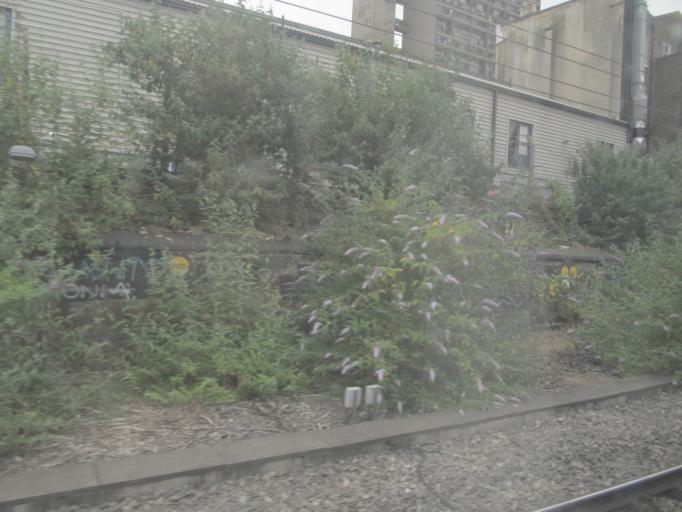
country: GB
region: England
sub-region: Greater London
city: Bayswater
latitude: 51.5232
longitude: -0.2081
